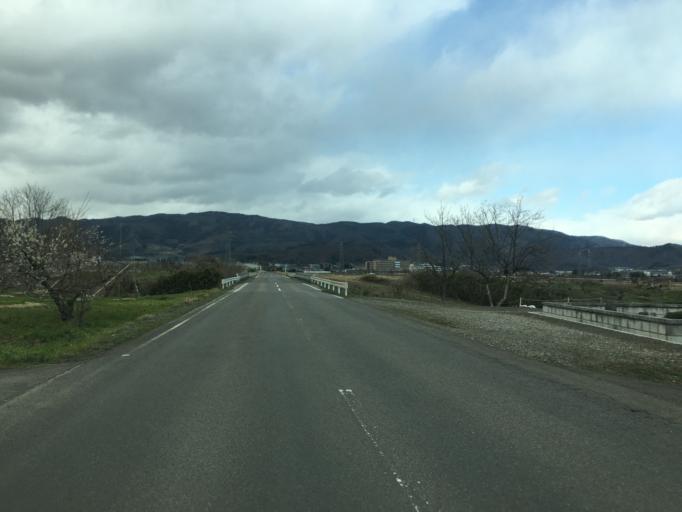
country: JP
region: Fukushima
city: Hobaramachi
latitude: 37.8623
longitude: 140.5380
